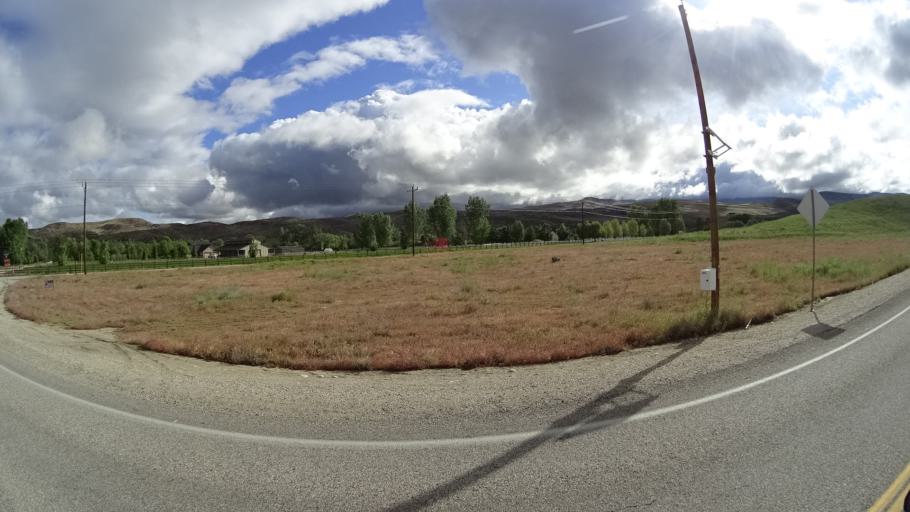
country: US
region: Idaho
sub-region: Ada County
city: Eagle
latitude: 43.7291
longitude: -116.2682
